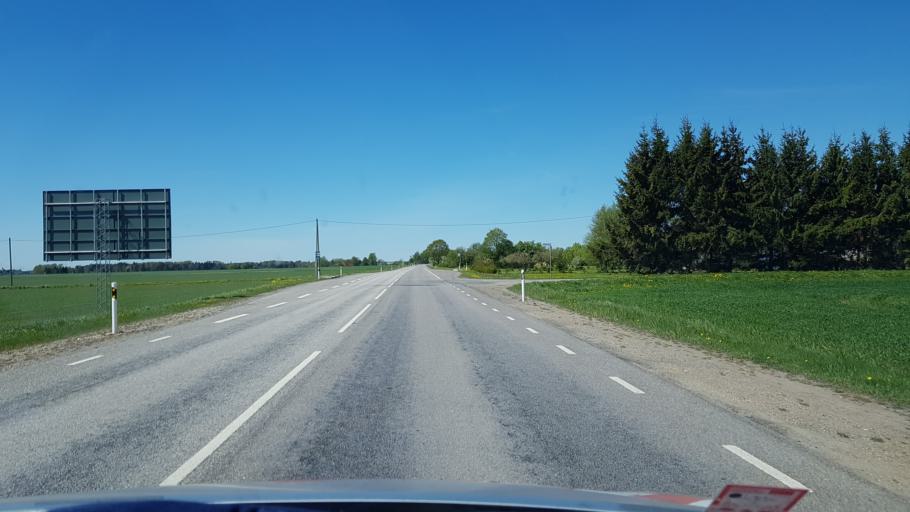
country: EE
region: Tartu
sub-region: Tartu linn
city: Tartu
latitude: 58.3793
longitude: 26.6720
